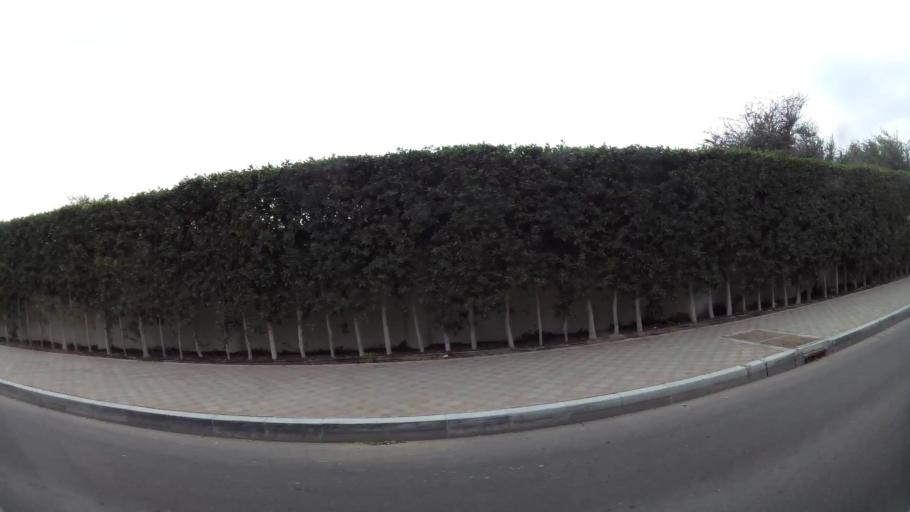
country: AE
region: Abu Dhabi
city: Abu Dhabi
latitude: 24.4170
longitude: 54.4232
